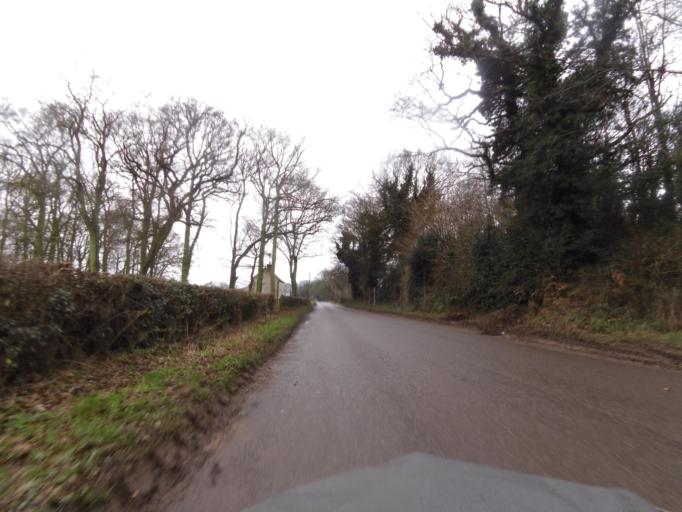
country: GB
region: England
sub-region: Norfolk
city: Briston
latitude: 52.8857
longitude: 1.0818
